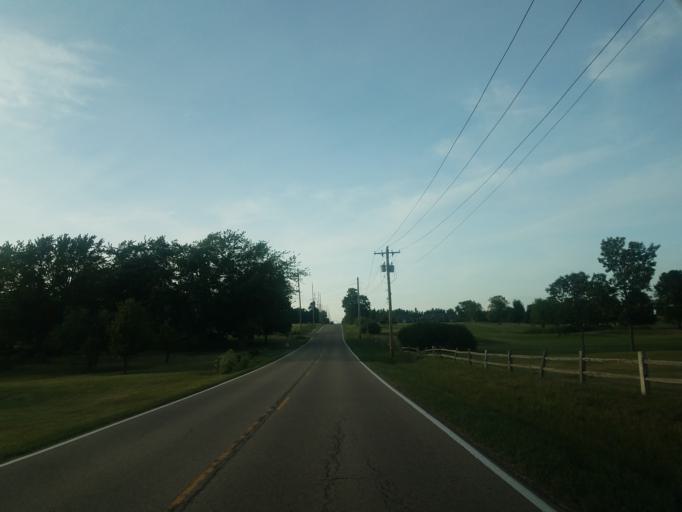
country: US
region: Illinois
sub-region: McLean County
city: Bloomington
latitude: 40.4433
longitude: -89.0055
